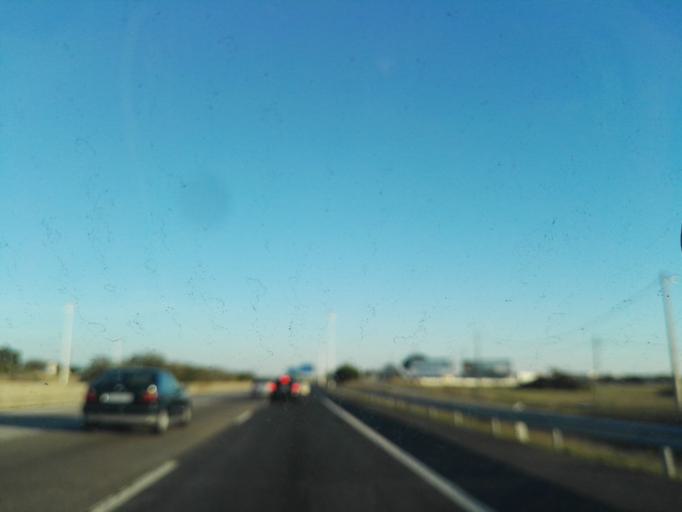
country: PT
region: Setubal
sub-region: Montijo
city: Montijo
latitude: 38.7216
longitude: -8.9643
